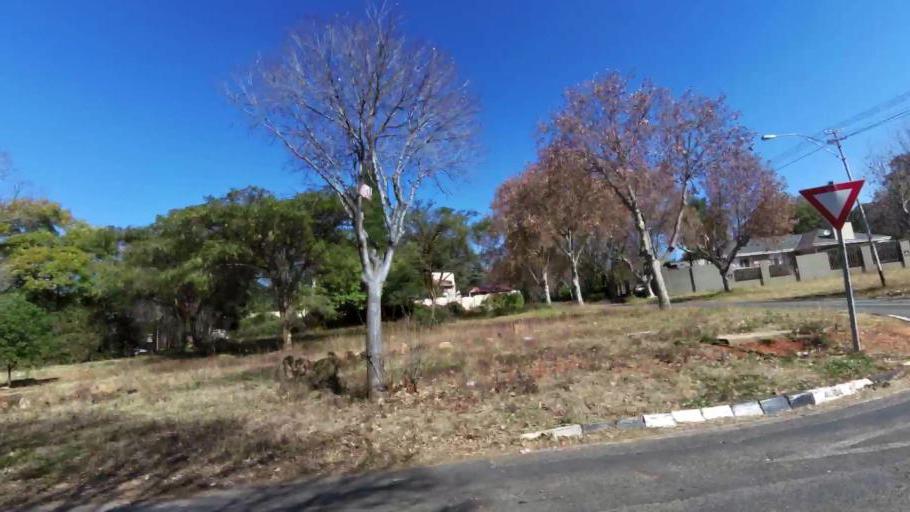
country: ZA
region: Gauteng
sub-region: City of Johannesburg Metropolitan Municipality
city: Johannesburg
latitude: -26.1466
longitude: 27.9806
